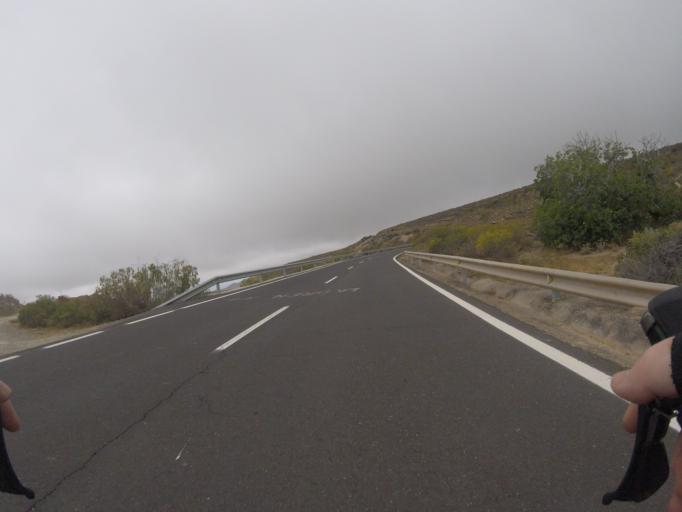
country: ES
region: Canary Islands
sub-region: Provincia de Santa Cruz de Tenerife
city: Fasnia
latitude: 28.2006
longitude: -16.4594
